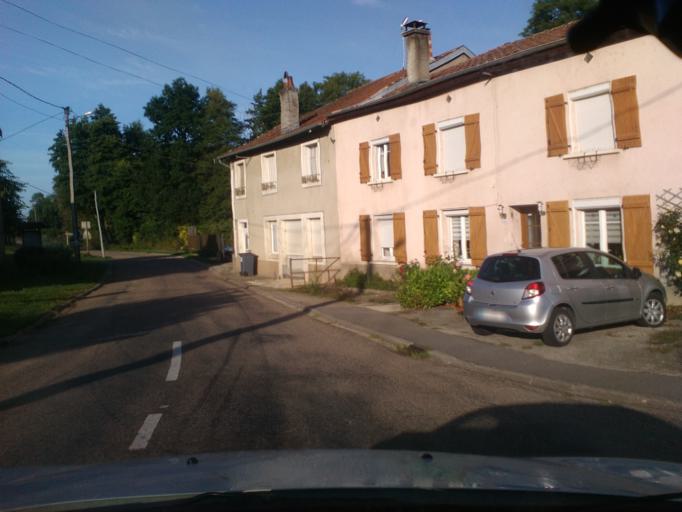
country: FR
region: Lorraine
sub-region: Departement des Vosges
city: Mirecourt
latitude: 48.2921
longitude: 6.0722
